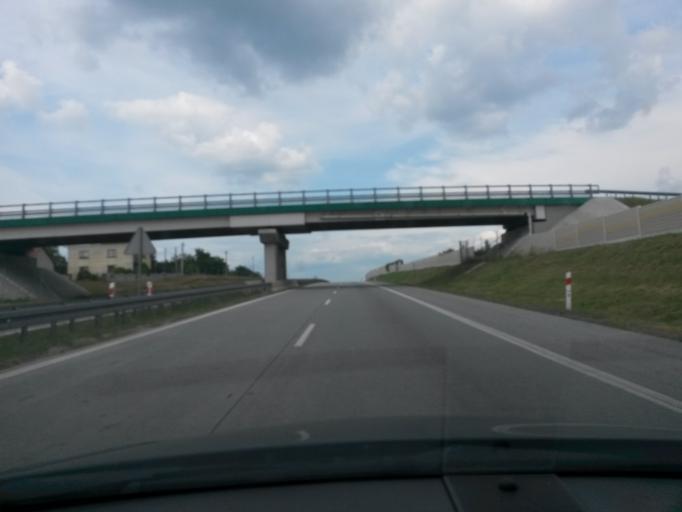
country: PL
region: Lodz Voivodeship
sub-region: Powiat skierniewicki
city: Kowiesy
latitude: 51.8792
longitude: 20.3960
